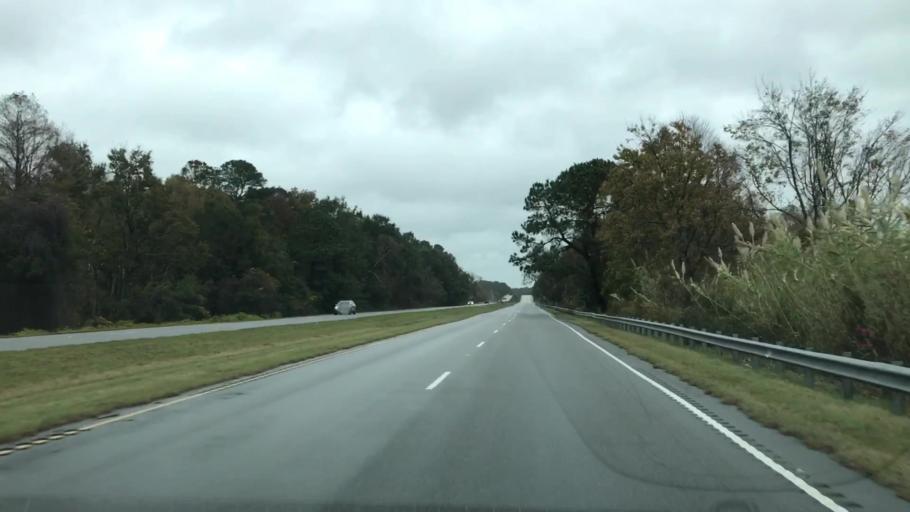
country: US
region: South Carolina
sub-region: Georgetown County
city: Georgetown
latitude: 33.2020
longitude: -79.3902
